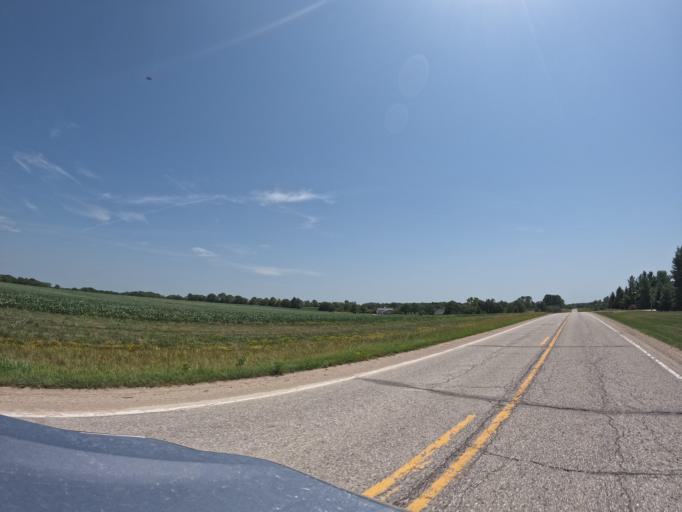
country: US
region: Iowa
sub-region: Henry County
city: Mount Pleasant
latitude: 40.9547
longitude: -91.6125
